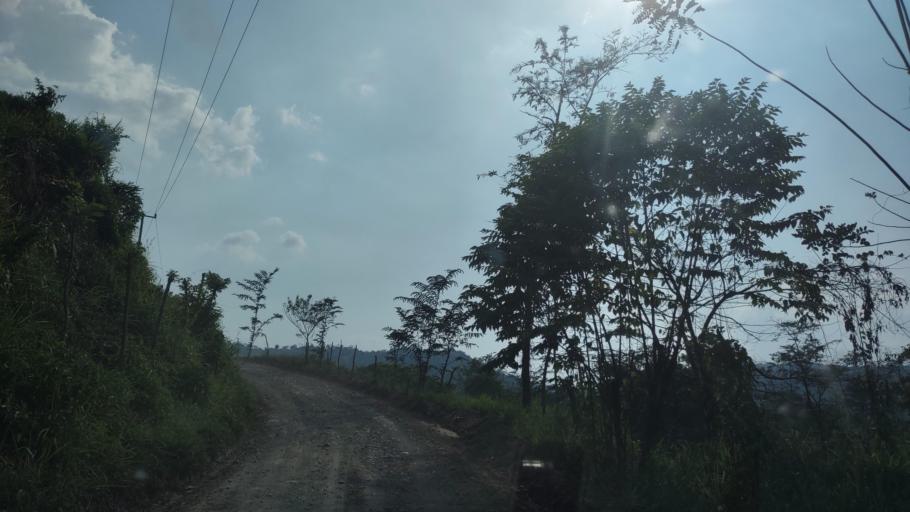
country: MX
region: Chiapas
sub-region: Tecpatan
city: Raudales Malpaso
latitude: 17.3175
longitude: -93.7415
